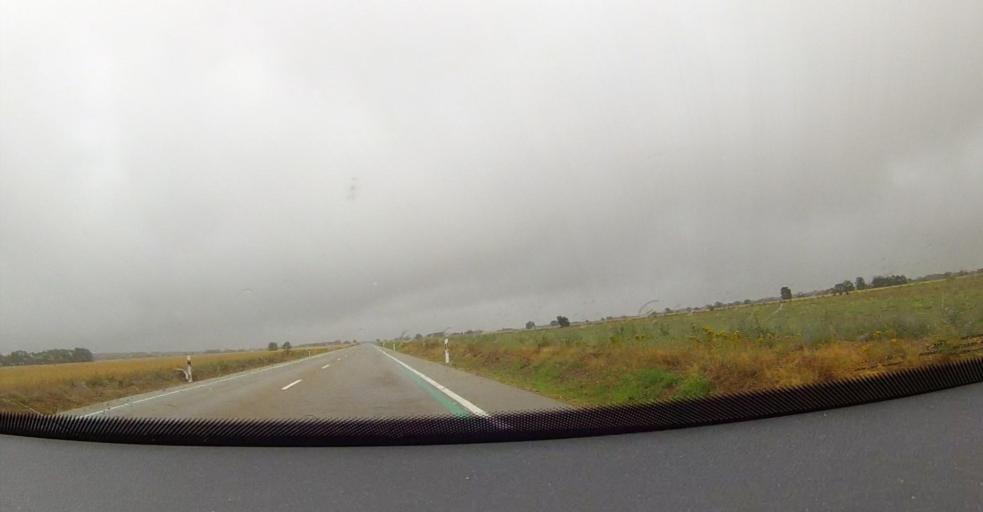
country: ES
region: Castille and Leon
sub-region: Provincia de Palencia
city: Poza de la Vega
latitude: 42.6020
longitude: -4.7637
